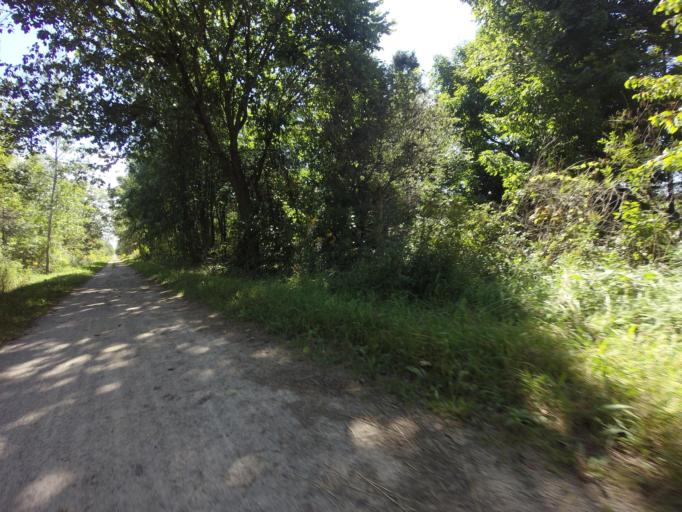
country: CA
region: Ontario
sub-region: Wellington County
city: Guelph
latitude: 43.7383
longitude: -80.3514
